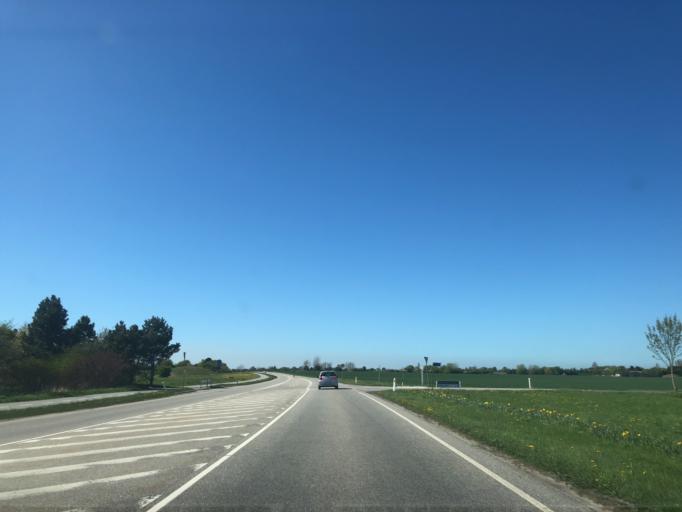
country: DK
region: Zealand
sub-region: Stevns Kommune
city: Store Heddinge
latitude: 55.3495
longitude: 12.3328
